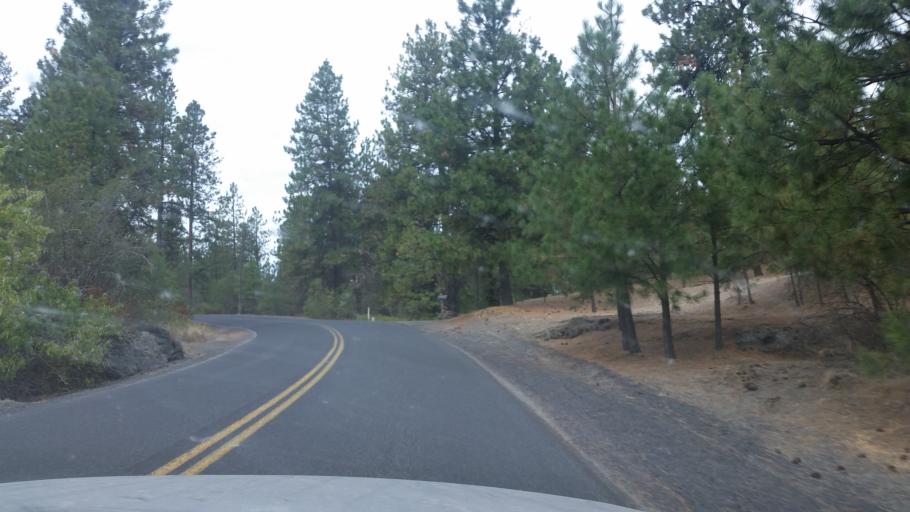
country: US
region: Washington
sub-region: Spokane County
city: Spokane
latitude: 47.6552
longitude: -117.4877
